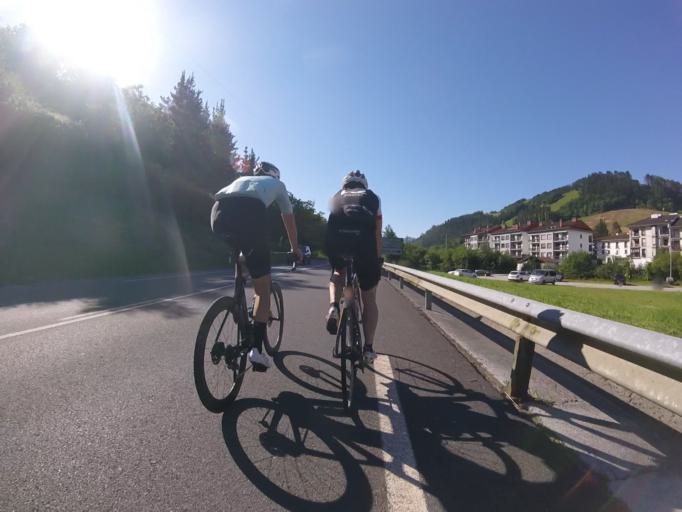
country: ES
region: Basque Country
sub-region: Provincia de Guipuzcoa
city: Azpeitia
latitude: 43.1578
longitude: -2.2435
